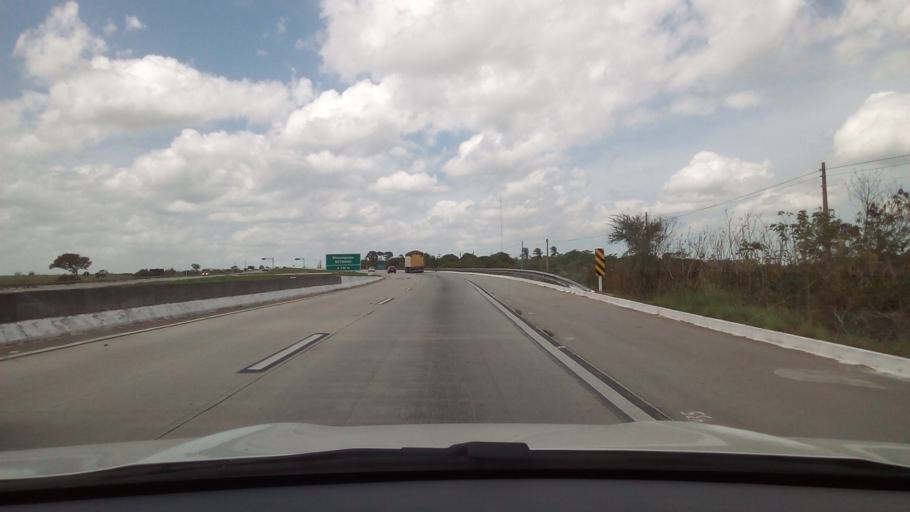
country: BR
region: Paraiba
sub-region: Mamanguape
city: Mamanguape
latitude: -6.8178
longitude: -35.1387
